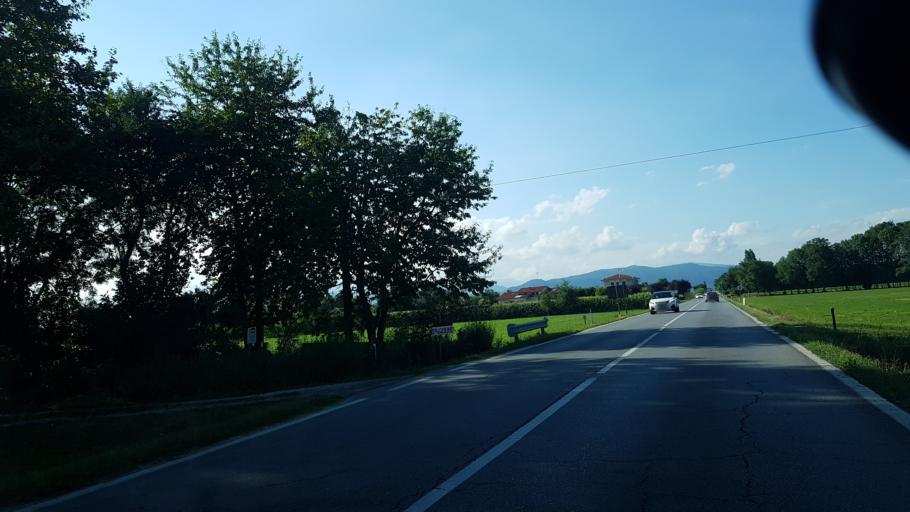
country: IT
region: Piedmont
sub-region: Provincia di Cuneo
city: Roata Rossi
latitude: 44.4493
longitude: 7.5263
